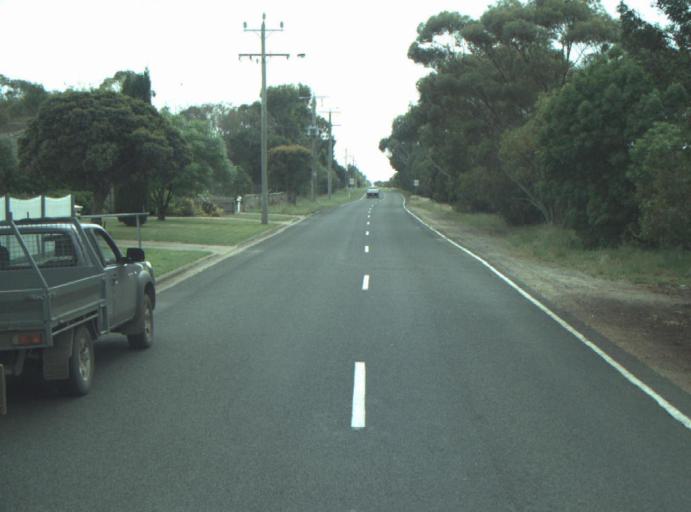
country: AU
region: Victoria
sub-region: Greater Geelong
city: Lara
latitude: -38.0174
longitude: 144.4186
